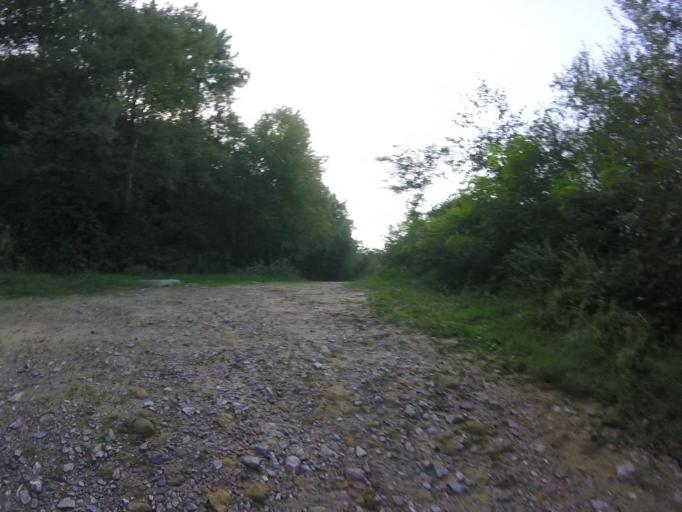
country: ES
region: Basque Country
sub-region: Provincia de Guipuzcoa
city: Fuenterrabia
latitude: 43.3659
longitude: -1.8249
